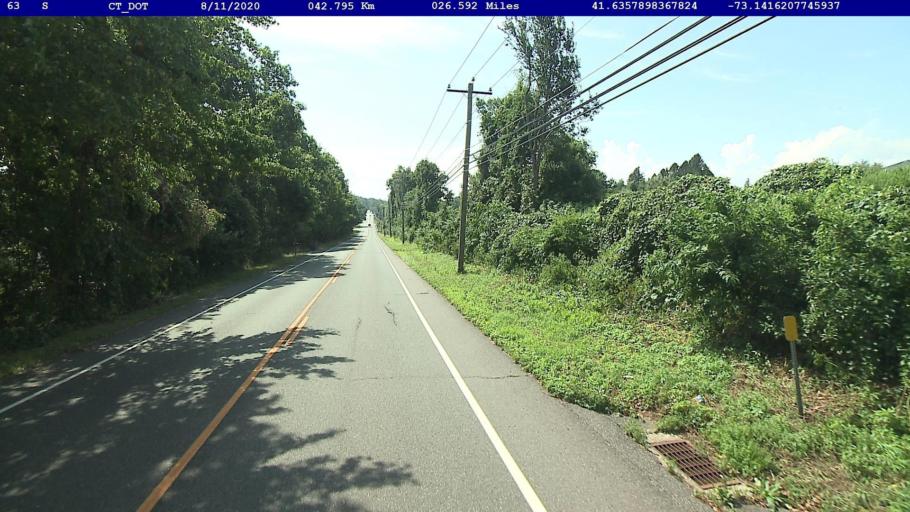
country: US
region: Connecticut
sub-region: Litchfield County
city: Watertown
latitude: 41.6358
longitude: -73.1417
